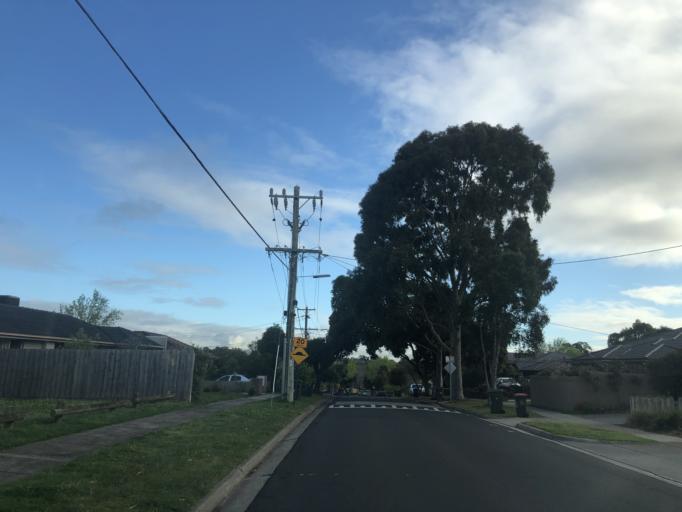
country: AU
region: Victoria
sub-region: Monash
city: Chadstone
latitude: -37.8876
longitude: 145.1149
